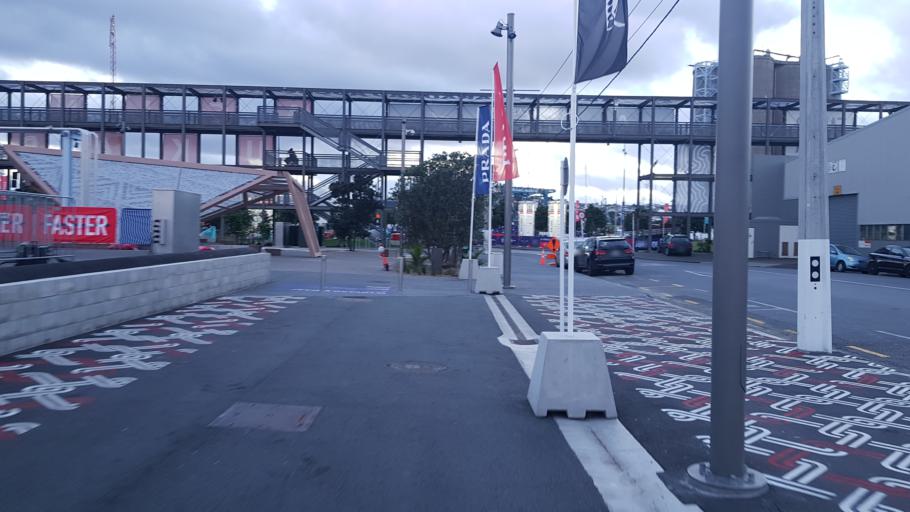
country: NZ
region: Auckland
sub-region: Auckland
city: Auckland
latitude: -36.8393
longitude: 174.7556
